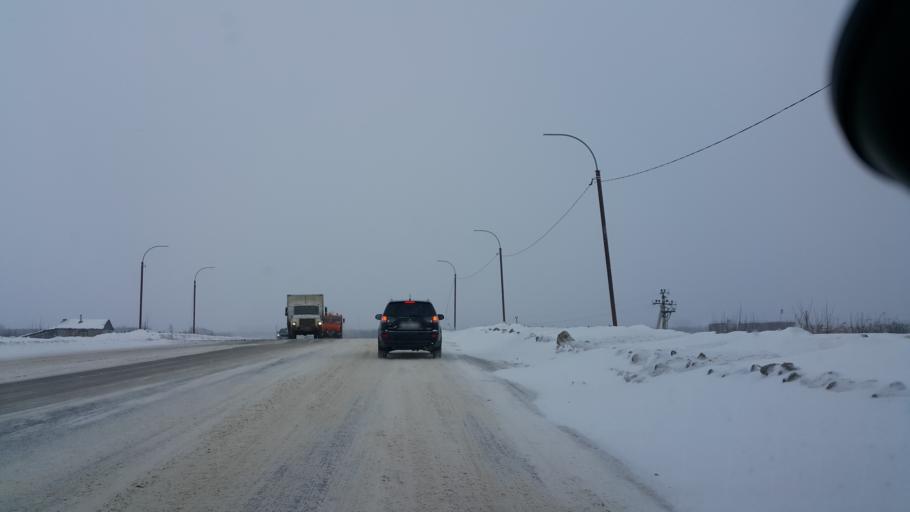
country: RU
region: Tambov
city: Tambov
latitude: 52.7392
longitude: 41.3777
